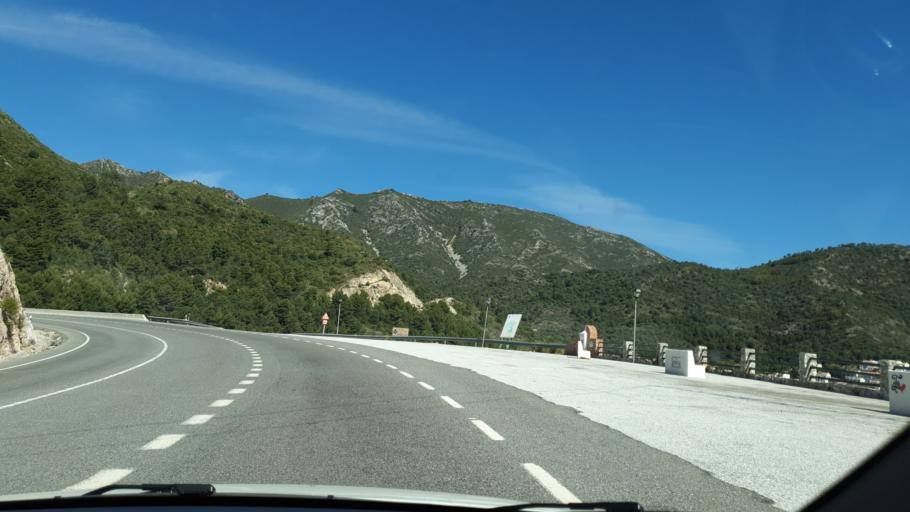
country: ES
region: Andalusia
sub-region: Provincia de Malaga
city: Ojen
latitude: 36.5596
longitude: -4.8609
